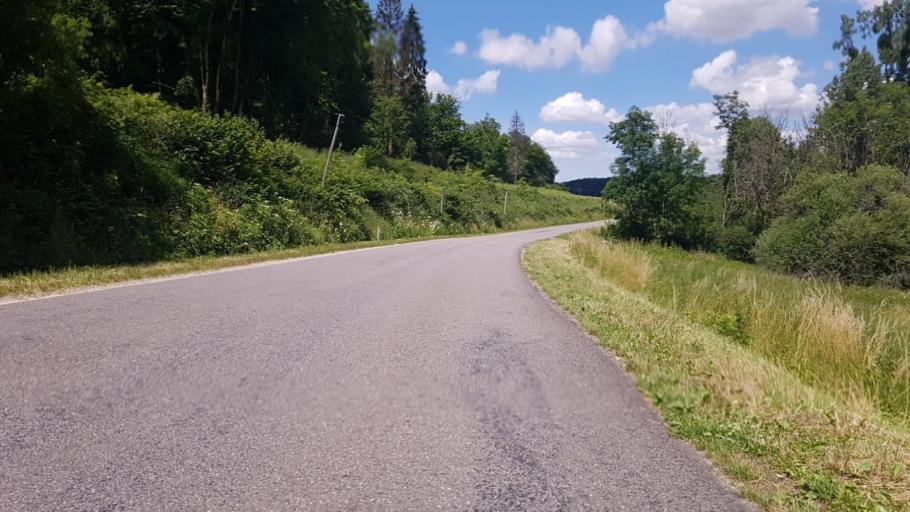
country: FR
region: Lorraine
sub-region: Departement de la Meuse
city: Gondrecourt-le-Chateau
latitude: 48.6338
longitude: 5.4527
